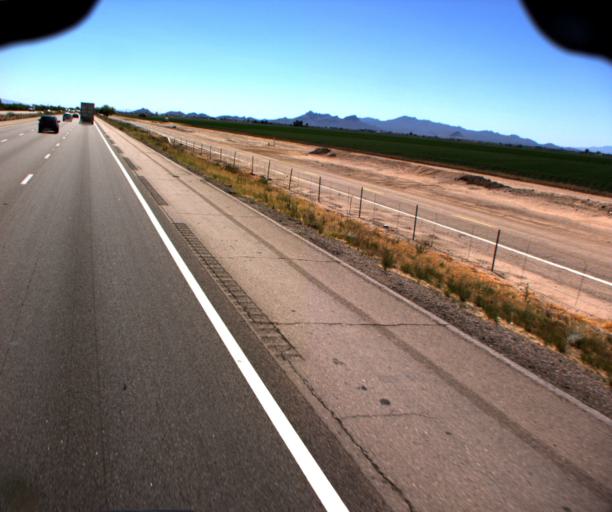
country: US
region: Arizona
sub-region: Pima County
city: Marana
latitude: 32.4809
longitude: -111.2431
